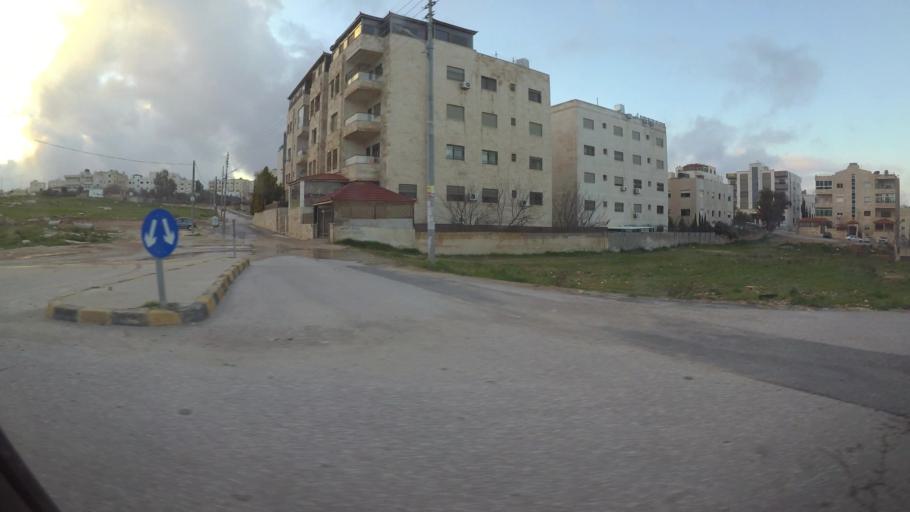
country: JO
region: Amman
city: Al Jubayhah
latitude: 32.0448
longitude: 35.9003
